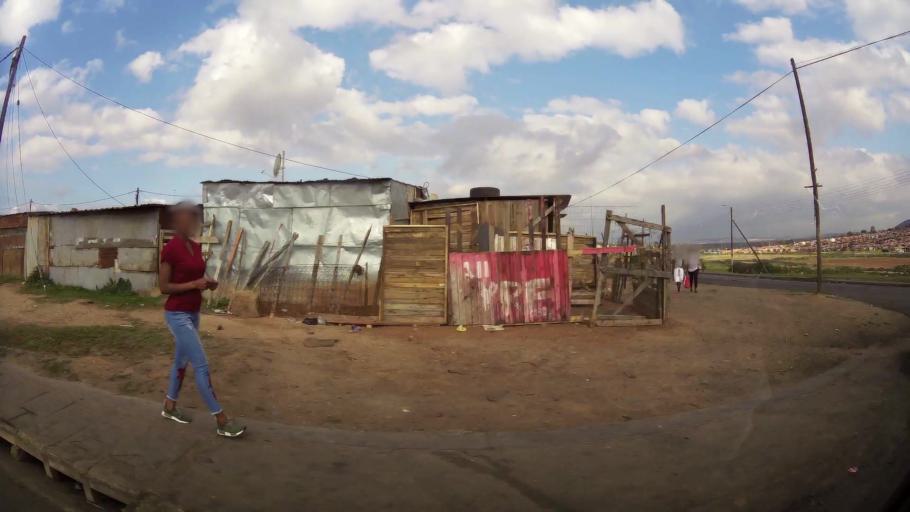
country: ZA
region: Eastern Cape
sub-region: Nelson Mandela Bay Metropolitan Municipality
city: Uitenhage
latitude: -33.7484
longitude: 25.3910
